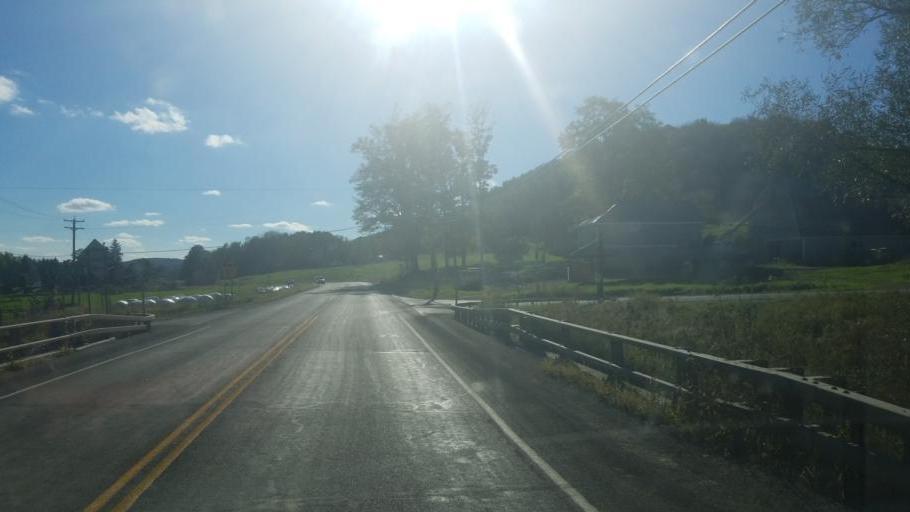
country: US
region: New York
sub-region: Allegany County
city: Cuba
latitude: 42.2676
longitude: -78.2530
